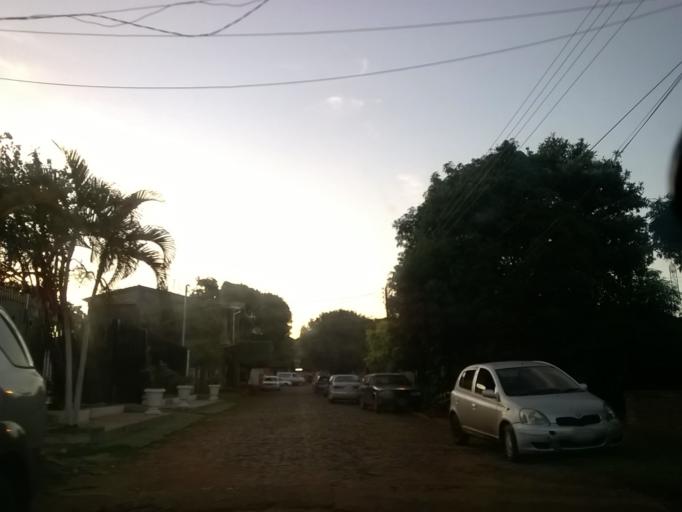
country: PY
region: Alto Parana
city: Ciudad del Este
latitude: -25.4770
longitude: -54.6493
